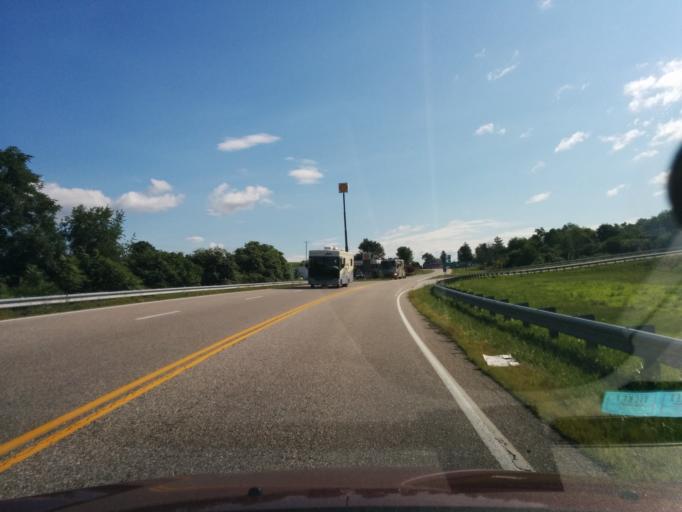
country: US
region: Virginia
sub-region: Rockbridge County
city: Glasgow
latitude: 37.6730
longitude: -79.5053
